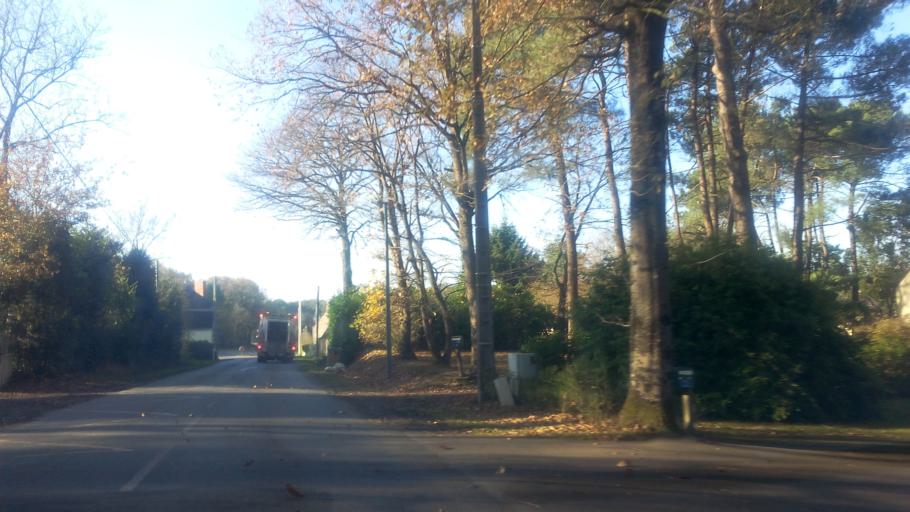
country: FR
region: Pays de la Loire
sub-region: Departement de la Loire-Atlantique
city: Avessac
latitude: 47.6411
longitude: -2.0109
